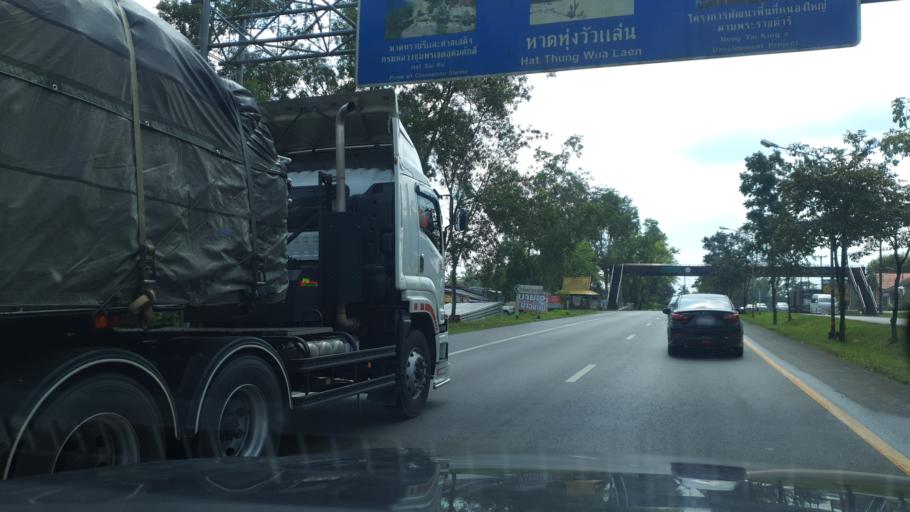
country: TH
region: Chumphon
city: Chumphon
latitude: 10.5505
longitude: 99.1179
